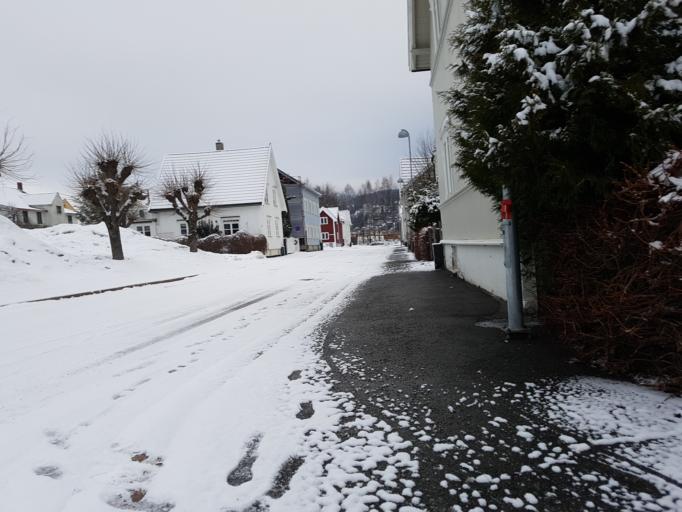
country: NO
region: Buskerud
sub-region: Drammen
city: Drammen
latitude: 59.7390
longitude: 10.1922
